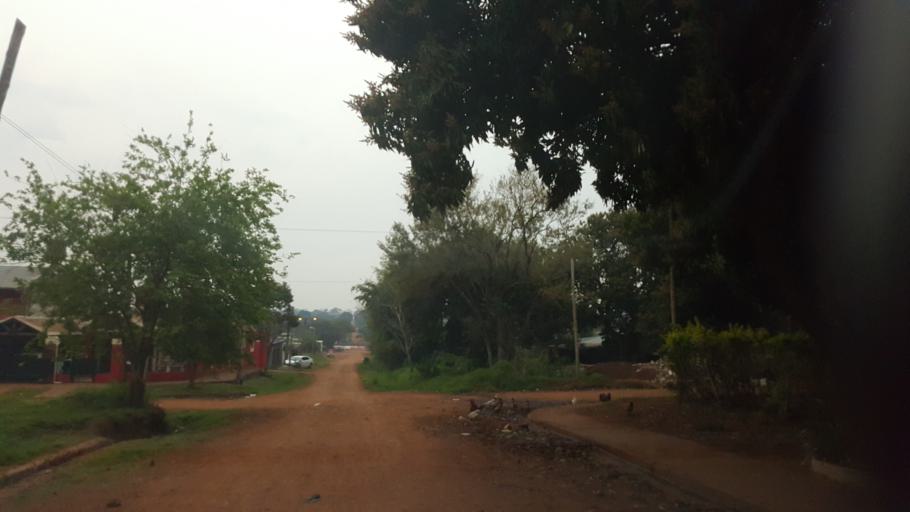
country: AR
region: Misiones
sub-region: Departamento de Capital
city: Posadas
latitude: -27.3965
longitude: -55.9301
